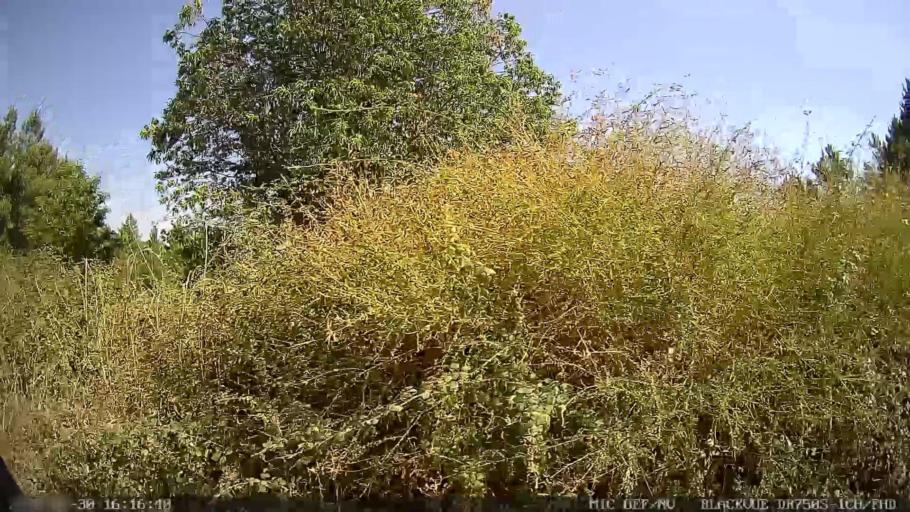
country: PT
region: Vila Real
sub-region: Murca
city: Murca
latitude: 41.3303
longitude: -7.4890
